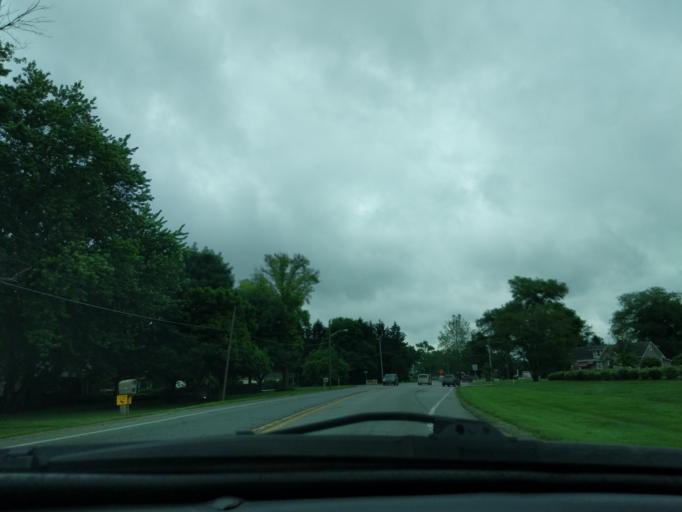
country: US
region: Indiana
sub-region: Hamilton County
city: Noblesville
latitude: 40.0515
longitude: -86.0283
